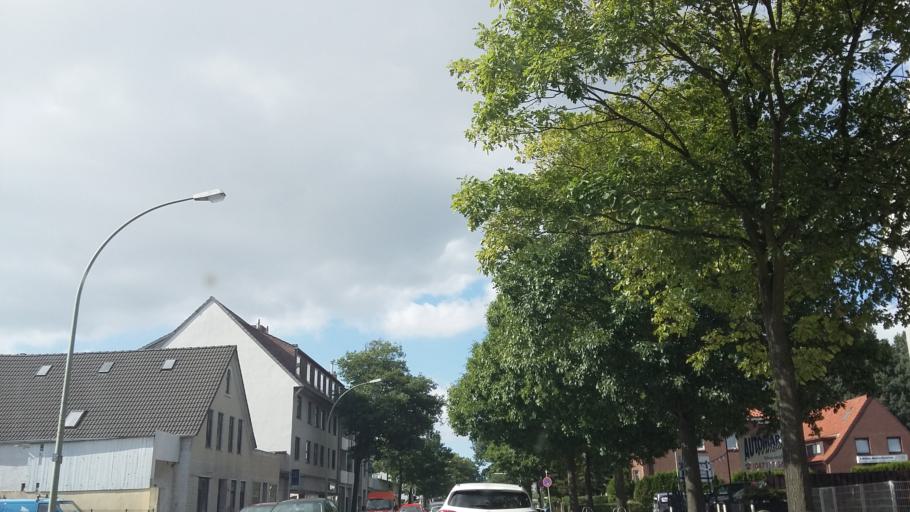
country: DE
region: Bremen
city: Bremerhaven
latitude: 53.5085
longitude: 8.5970
